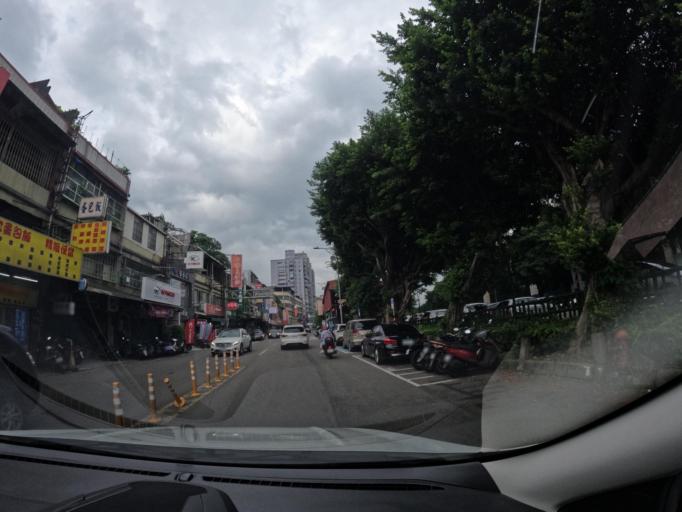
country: TW
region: Taiwan
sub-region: Taoyuan
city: Taoyuan
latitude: 24.9534
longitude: 121.3465
